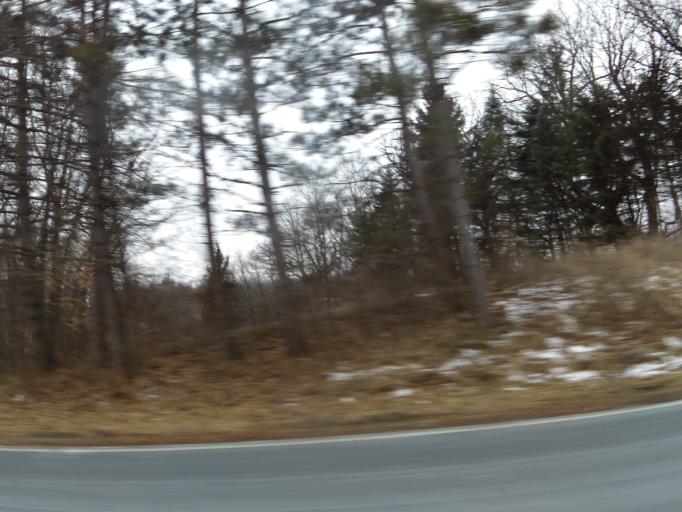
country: US
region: Minnesota
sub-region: Hennepin County
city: Long Lake
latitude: 45.0088
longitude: -93.5839
